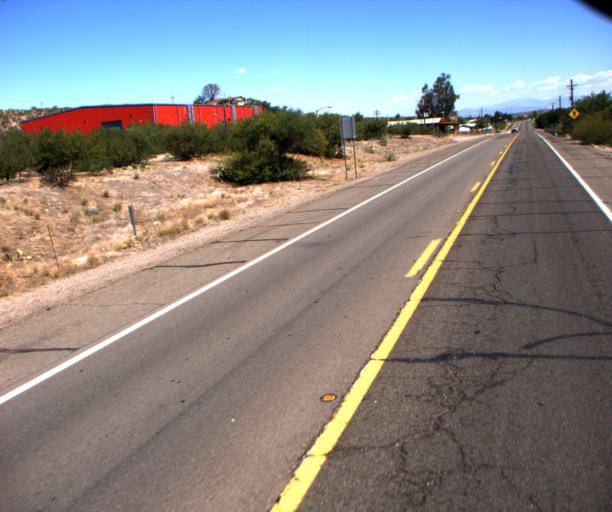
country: US
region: Arizona
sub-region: Pinal County
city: Mammoth
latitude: 32.7289
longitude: -110.6467
